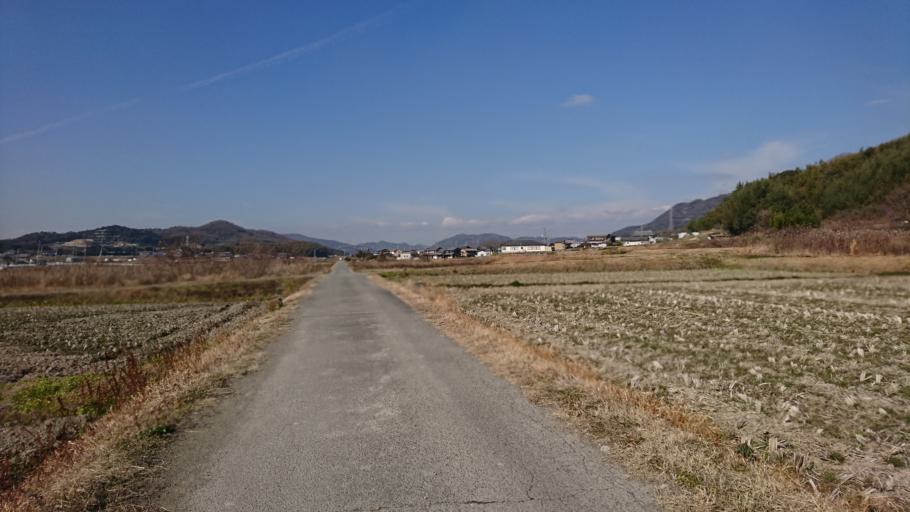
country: JP
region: Hyogo
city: Kakogawacho-honmachi
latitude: 34.8129
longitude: 134.8576
